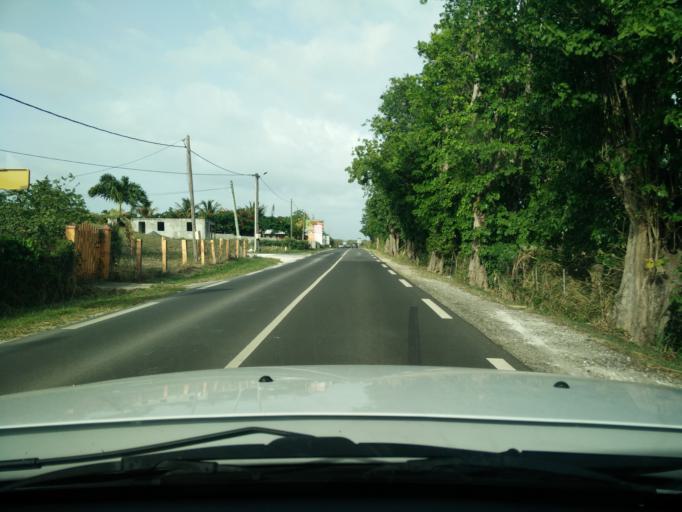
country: GP
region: Guadeloupe
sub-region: Guadeloupe
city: Saint-Francois
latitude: 16.2541
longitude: -61.3195
